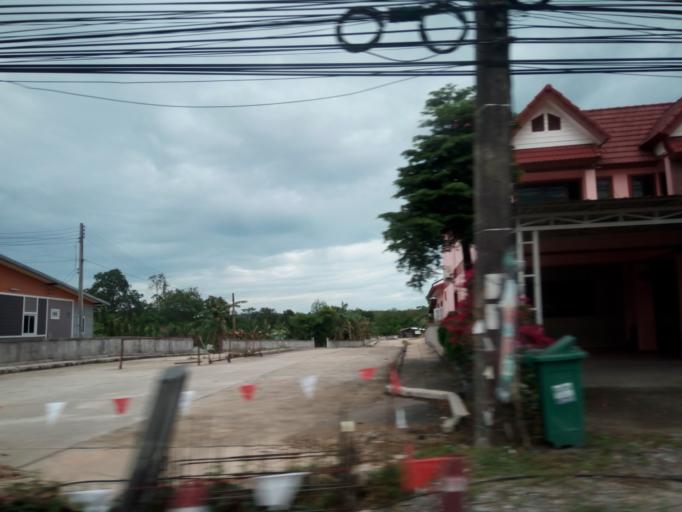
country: TH
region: Phuket
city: Thalang
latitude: 8.0922
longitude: 98.3391
